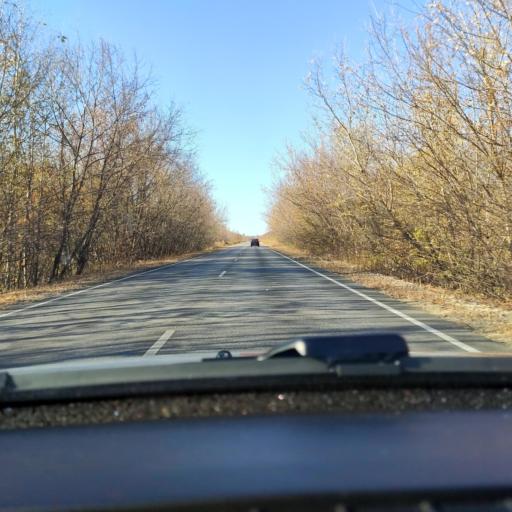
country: RU
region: Voronezj
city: Zemlyansk
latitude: 51.8370
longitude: 38.8167
